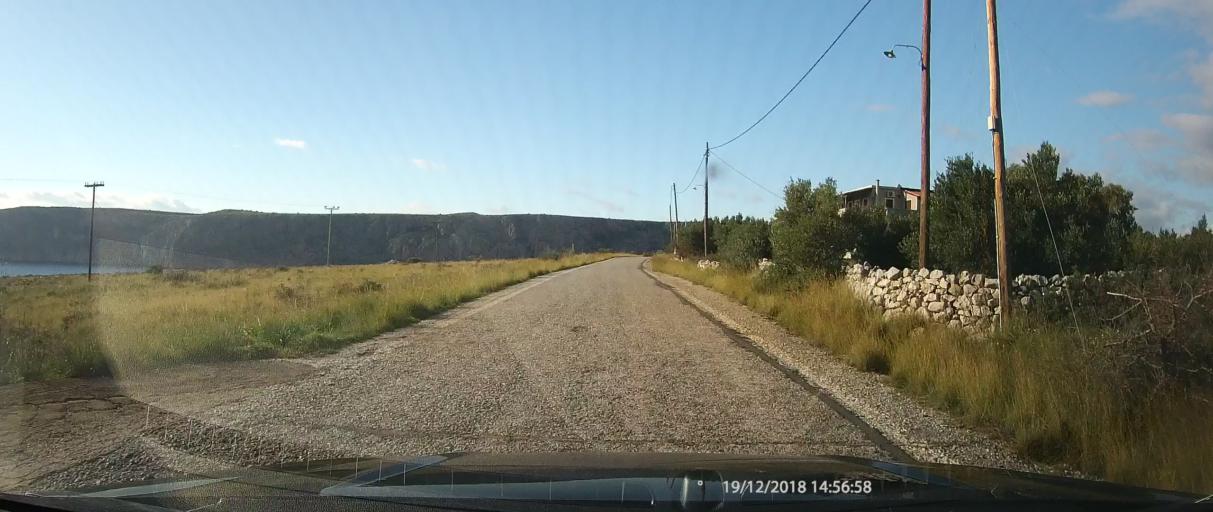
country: GR
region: Peloponnese
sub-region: Nomos Lakonias
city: Gytheio
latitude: 36.4791
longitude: 22.4116
